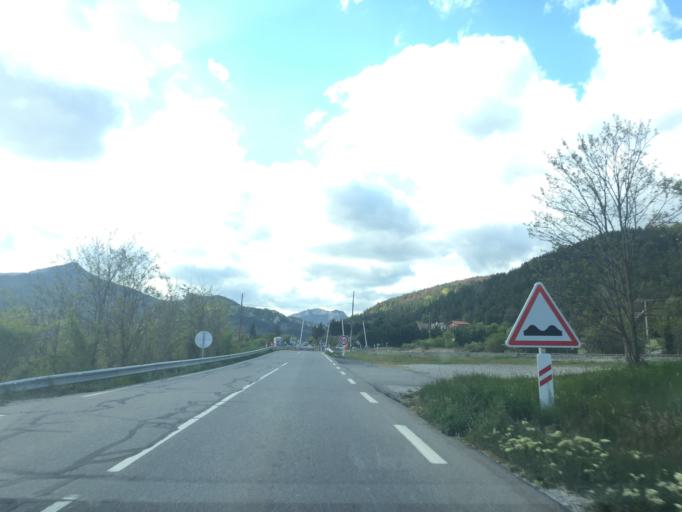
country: FR
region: Provence-Alpes-Cote d'Azur
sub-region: Departement des Hautes-Alpes
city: Serres
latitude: 44.4088
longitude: 5.7276
